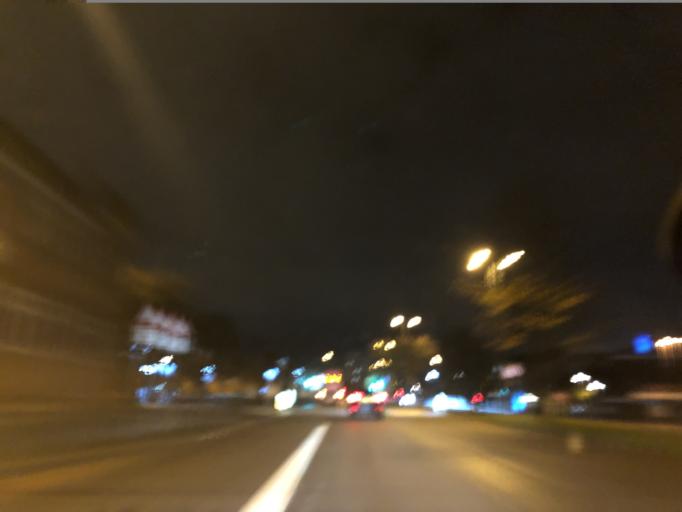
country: GB
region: England
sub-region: Borough of Oldham
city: Oldham
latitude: 53.5350
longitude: -2.1156
